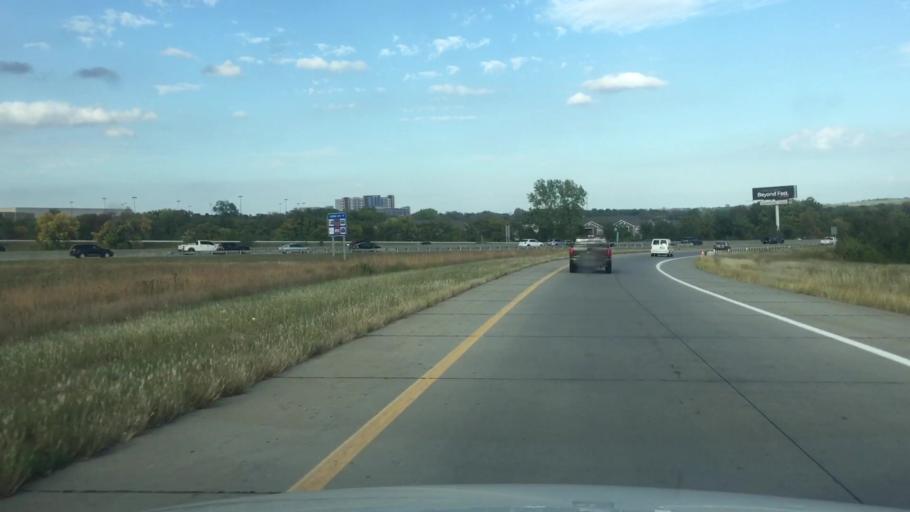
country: US
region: Missouri
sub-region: Jackson County
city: East Independence
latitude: 39.0403
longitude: -94.3591
